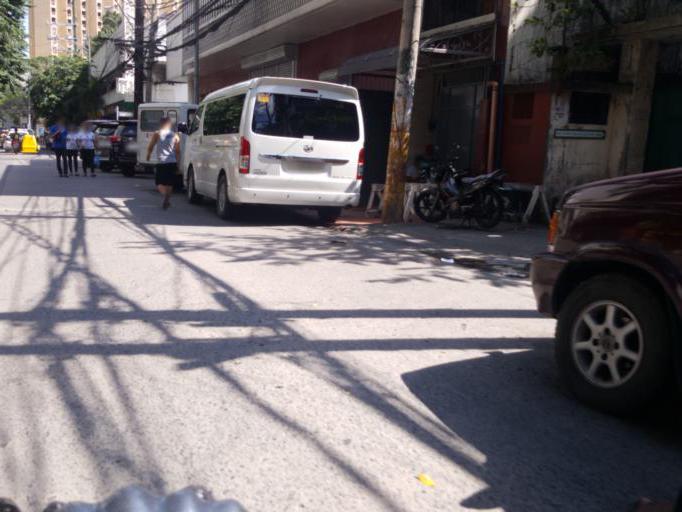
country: PH
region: Metro Manila
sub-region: City of Manila
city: Port Area
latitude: 14.5791
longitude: 120.9818
